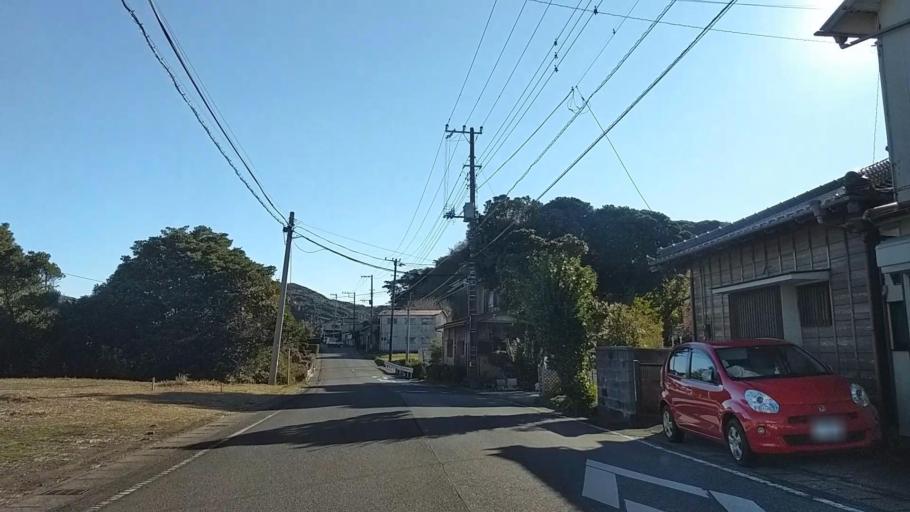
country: JP
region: Chiba
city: Futtsu
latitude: 35.2786
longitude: 139.8575
